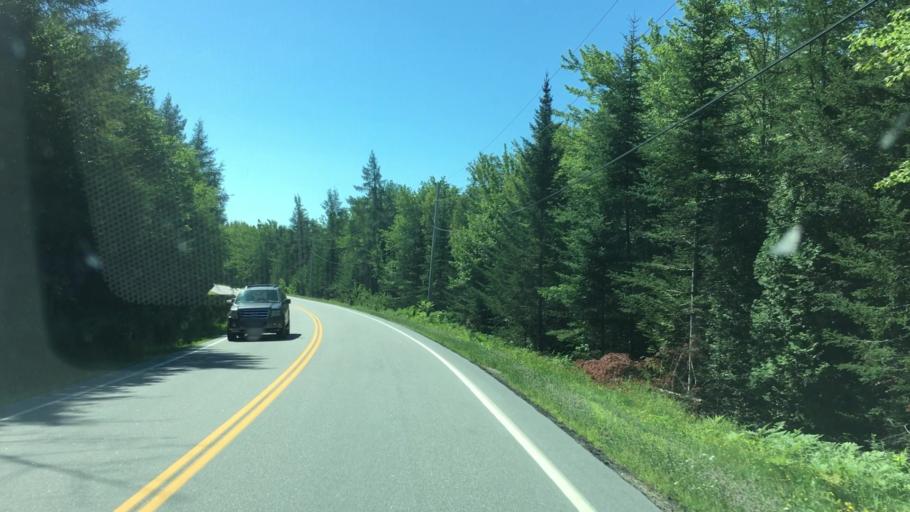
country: US
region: Maine
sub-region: Hancock County
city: Penobscot
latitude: 44.5038
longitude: -68.6549
